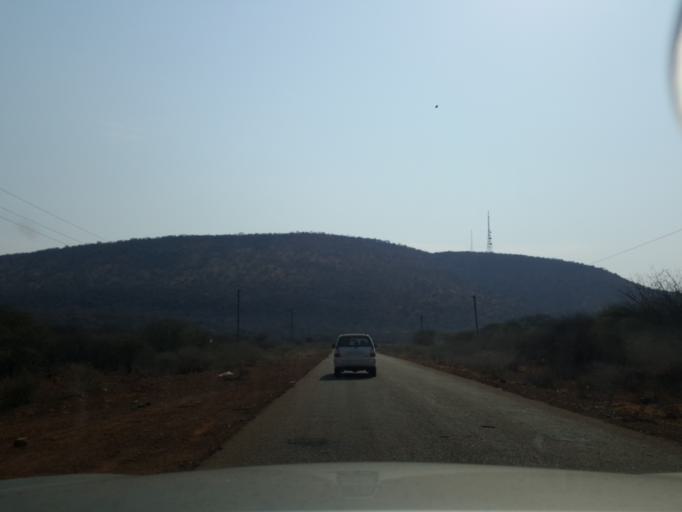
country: BW
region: South East
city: Lobatse
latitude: -25.2865
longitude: 25.8594
